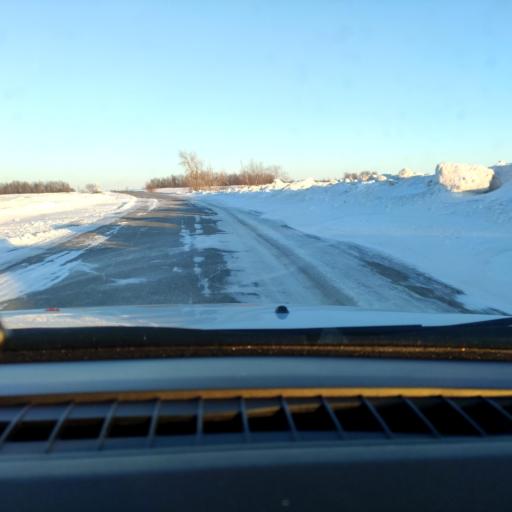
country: RU
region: Samara
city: Kinel'
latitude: 53.4374
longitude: 50.6678
